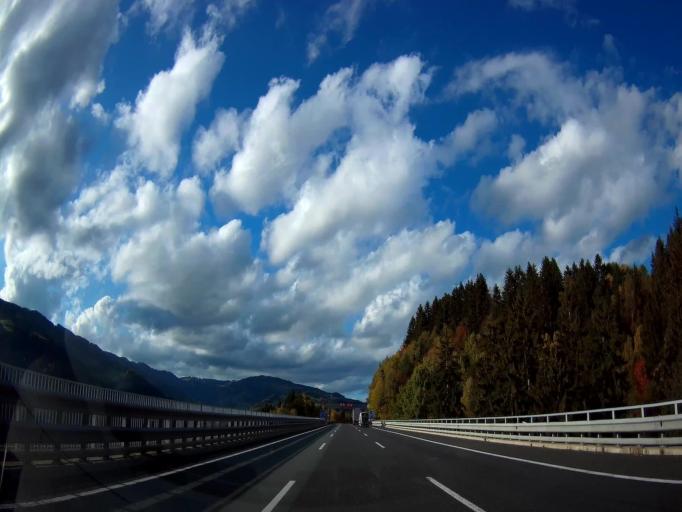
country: AT
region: Carinthia
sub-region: Politischer Bezirk Wolfsberg
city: Wolfsberg
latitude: 46.8913
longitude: 14.8230
